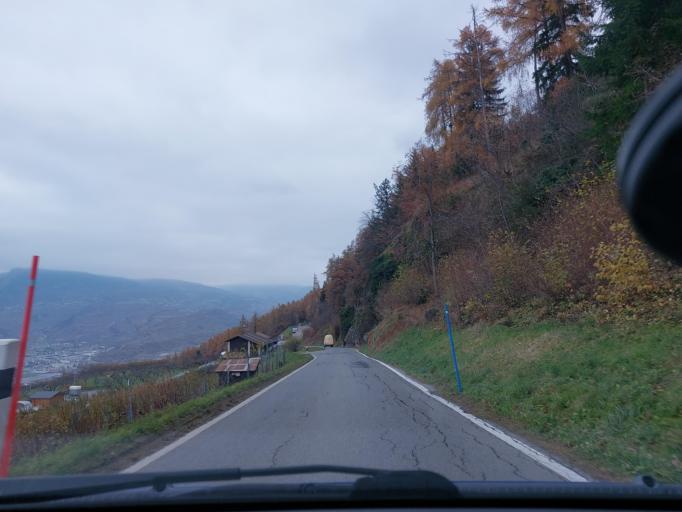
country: CH
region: Valais
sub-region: Conthey District
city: Basse-Nendaz
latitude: 46.1892
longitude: 7.2808
